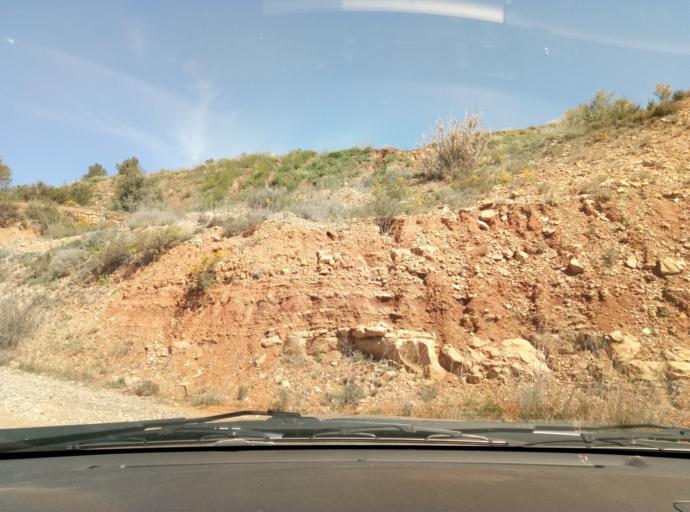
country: ES
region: Catalonia
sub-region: Provincia de Lleida
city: Juncosa
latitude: 41.4275
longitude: 0.8299
